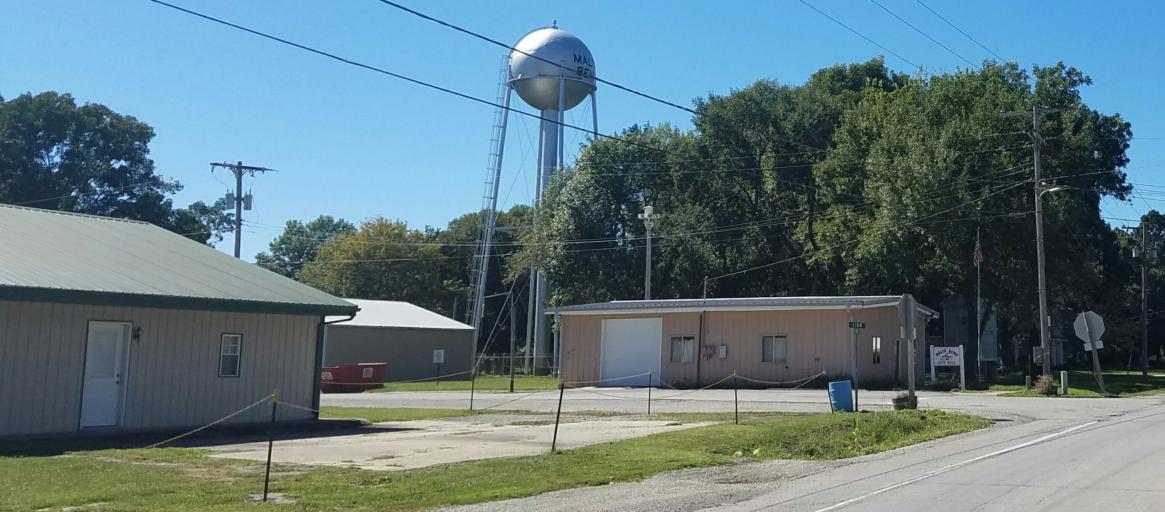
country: US
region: Missouri
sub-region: Saline County
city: Marshall
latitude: 39.1936
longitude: -93.3620
